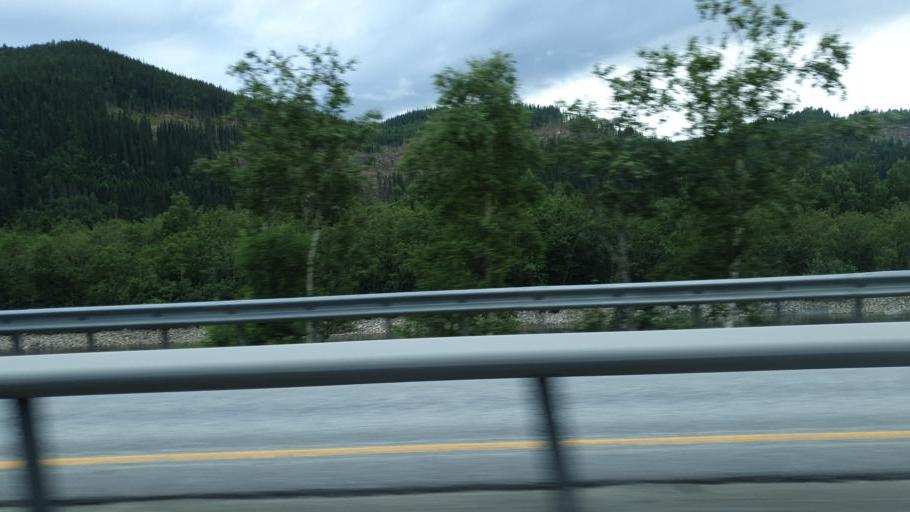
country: NO
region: Sor-Trondelag
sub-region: Midtre Gauldal
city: Storen
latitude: 63.0791
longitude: 10.2585
